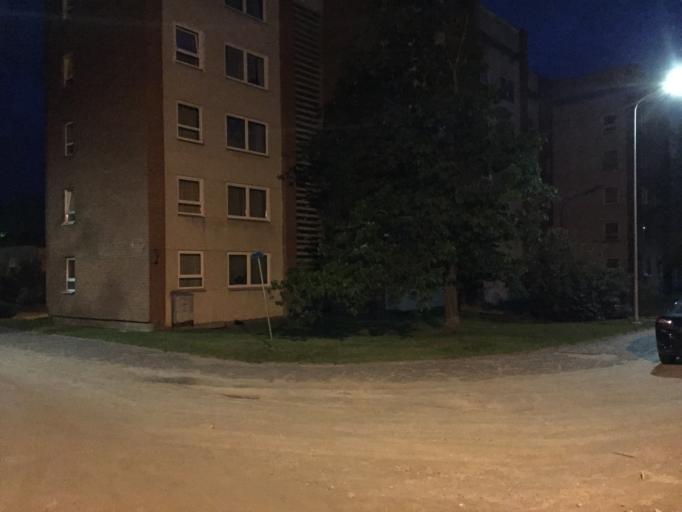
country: LV
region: Valmieras Rajons
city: Valmiera
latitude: 57.5257
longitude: 25.4385
